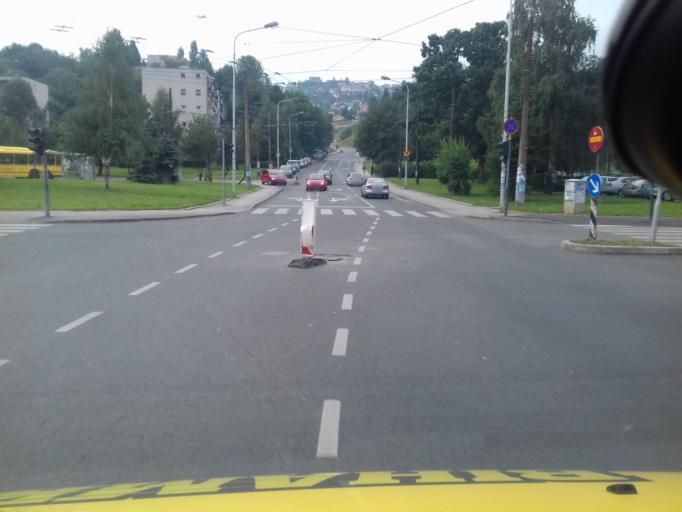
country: BA
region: Federation of Bosnia and Herzegovina
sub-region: Kanton Sarajevo
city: Sarajevo
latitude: 43.8480
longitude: 18.3671
